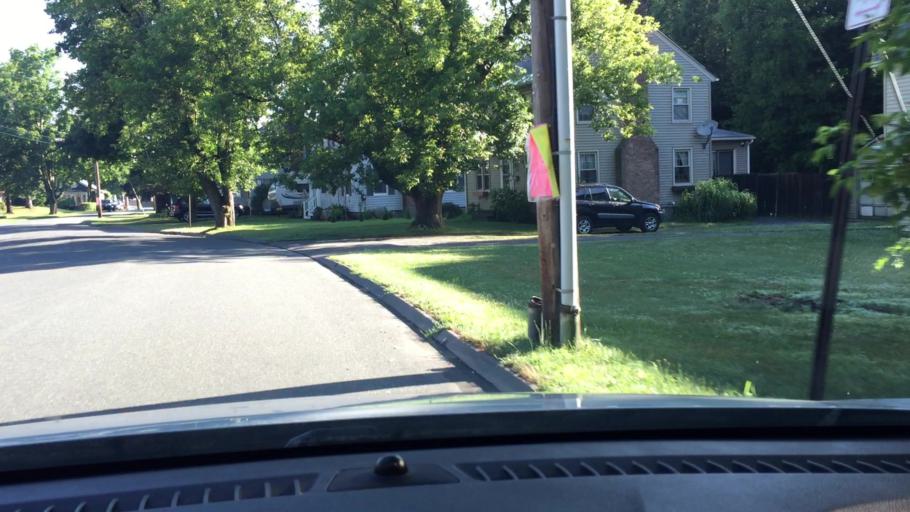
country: US
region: Massachusetts
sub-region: Berkshire County
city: Pittsfield
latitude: 42.4379
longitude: -73.2282
